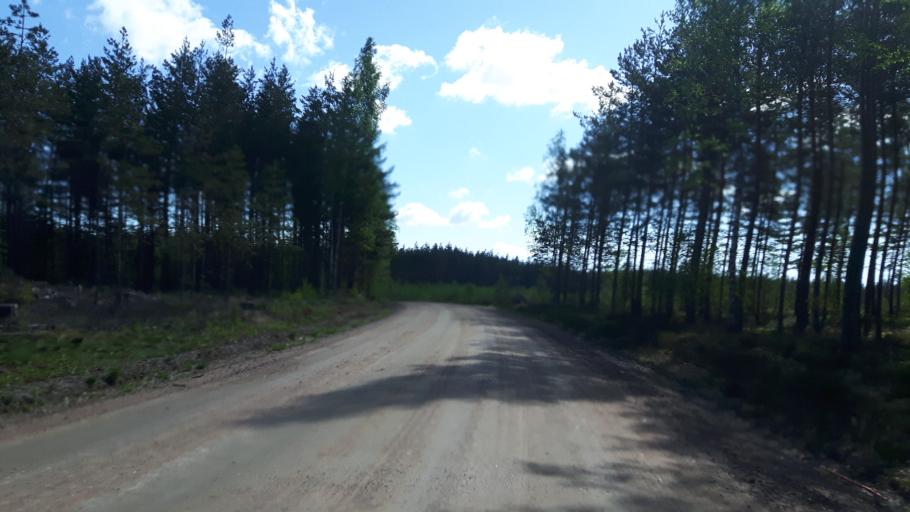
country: FI
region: Kymenlaakso
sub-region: Kotka-Hamina
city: Hamina
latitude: 60.5249
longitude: 27.2688
